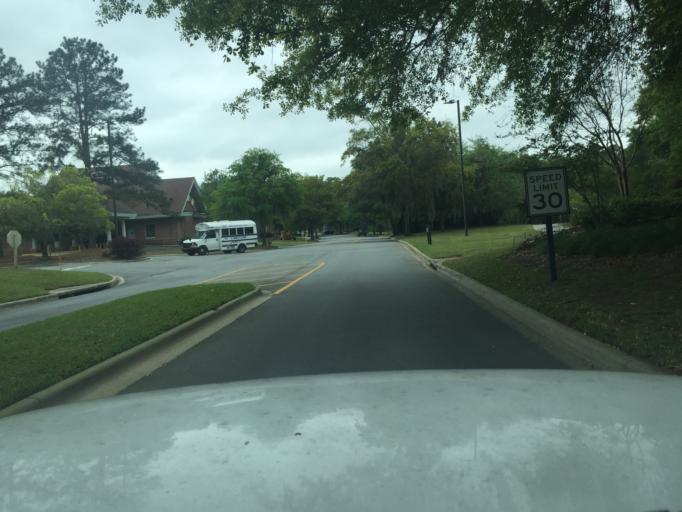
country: US
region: Georgia
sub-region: Chatham County
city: Skidaway Island
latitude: 31.9419
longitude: -81.0501
